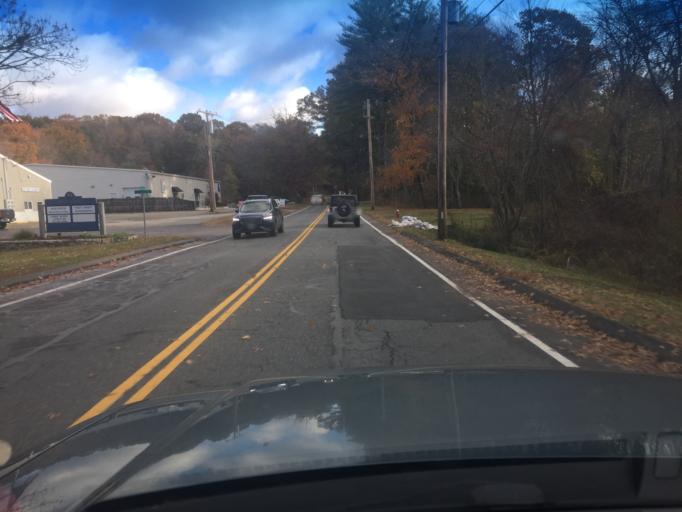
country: US
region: Massachusetts
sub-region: Norfolk County
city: Medfield
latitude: 42.1937
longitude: -71.3215
